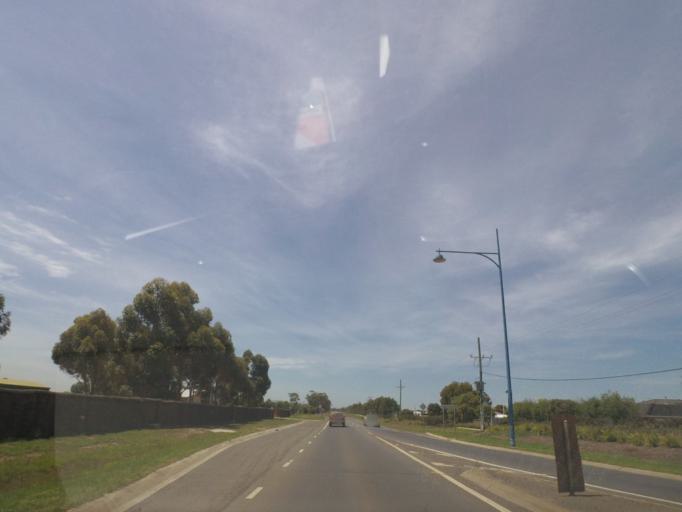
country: AU
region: Victoria
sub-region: Wyndham
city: Tarneit
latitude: -37.8771
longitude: 144.6172
